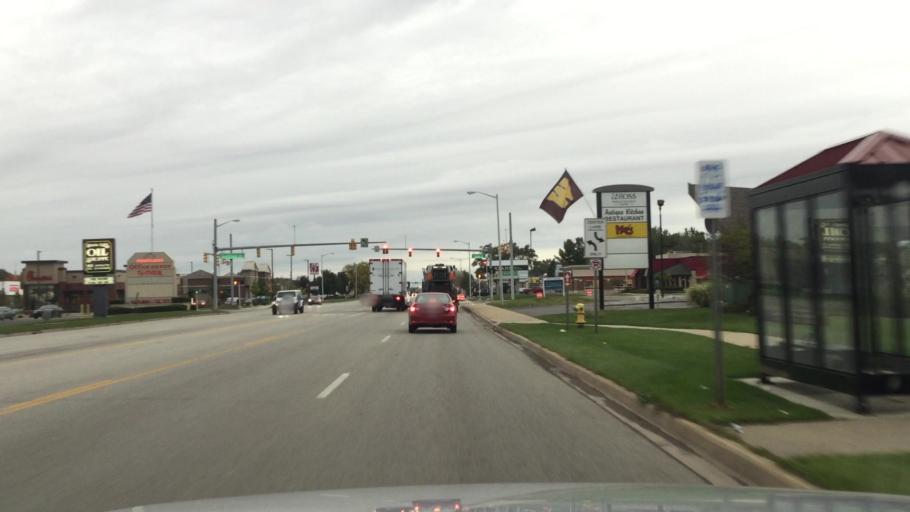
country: US
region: Michigan
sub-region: Kalamazoo County
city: Portage
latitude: 42.2261
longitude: -85.5894
